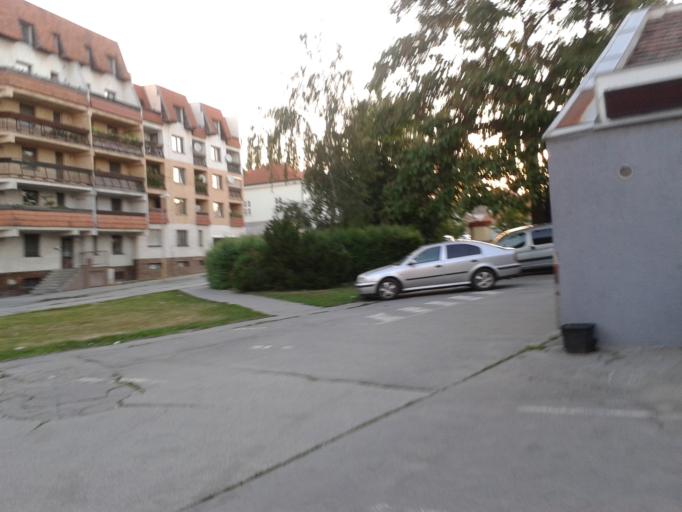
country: SK
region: Trnavsky
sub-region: Okres Trnava
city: Trnava
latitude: 48.3769
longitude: 17.5881
